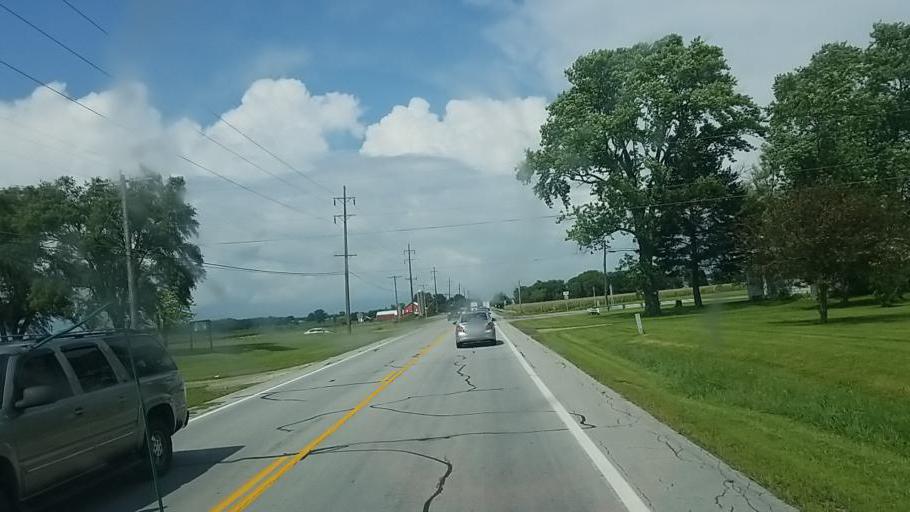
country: US
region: Ohio
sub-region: Champaign County
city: Urbana
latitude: 40.1545
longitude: -83.7459
